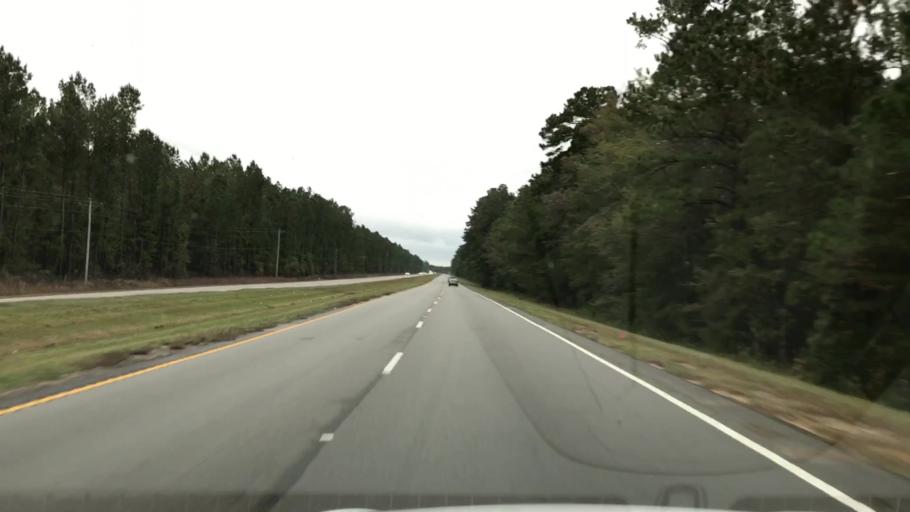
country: US
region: South Carolina
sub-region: Georgetown County
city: Georgetown
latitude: 33.2764
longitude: -79.3518
